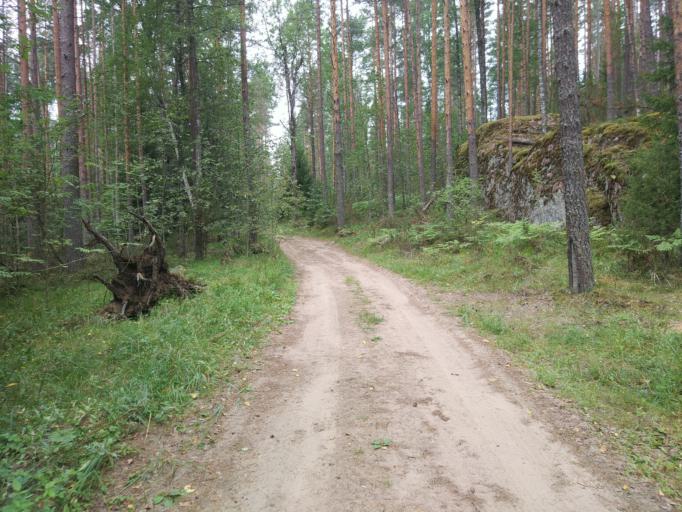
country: RU
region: Leningrad
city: Kuznechnoye
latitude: 61.0113
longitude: 29.6472
